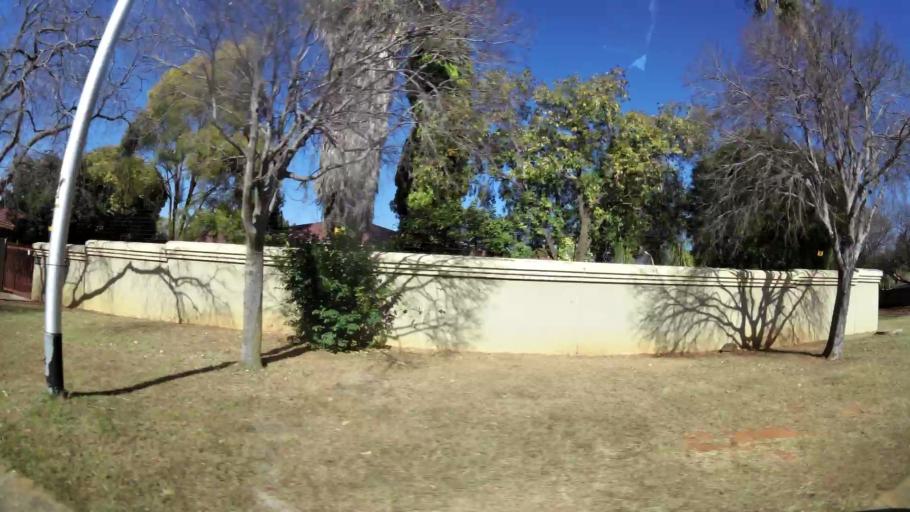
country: ZA
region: Gauteng
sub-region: City of Tshwane Metropolitan Municipality
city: Pretoria
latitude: -25.7248
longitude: 28.2435
